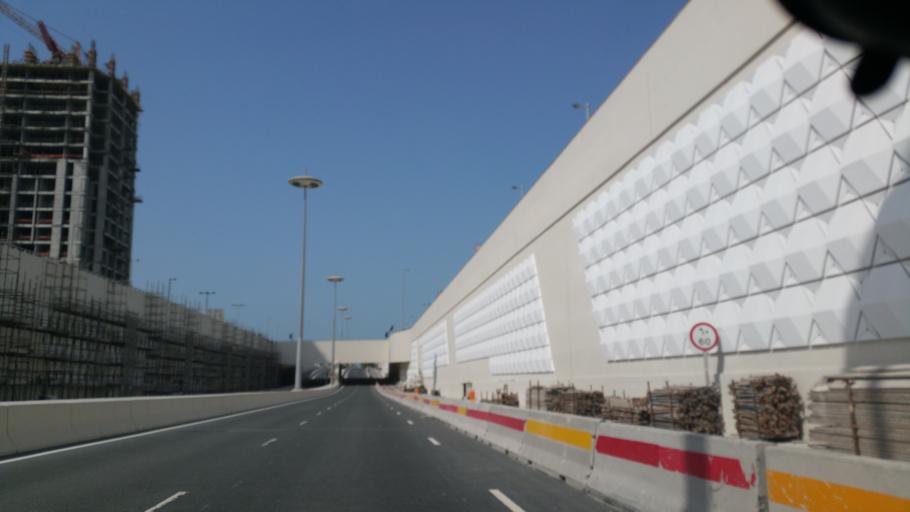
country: QA
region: Baladiyat Umm Salal
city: Umm Salal Muhammad
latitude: 25.4284
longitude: 51.5107
